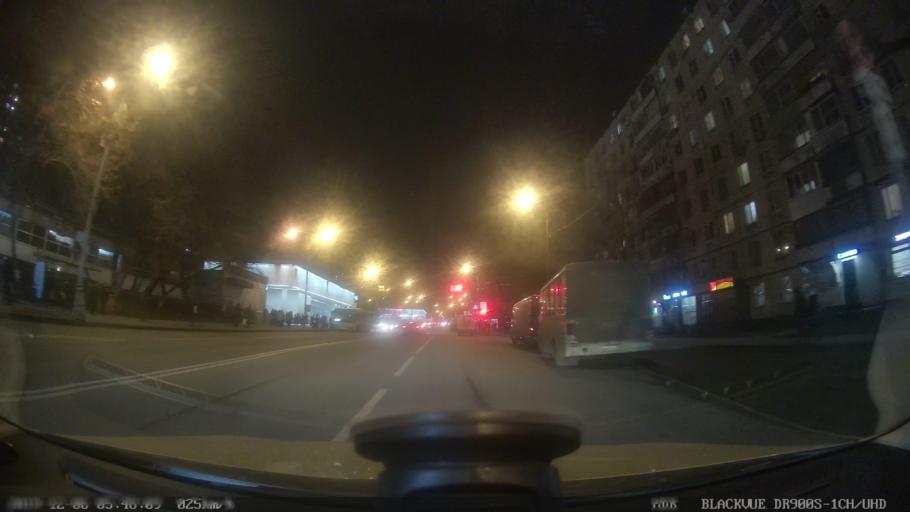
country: RU
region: Moscow
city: Vatutino
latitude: 55.8854
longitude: 37.6619
